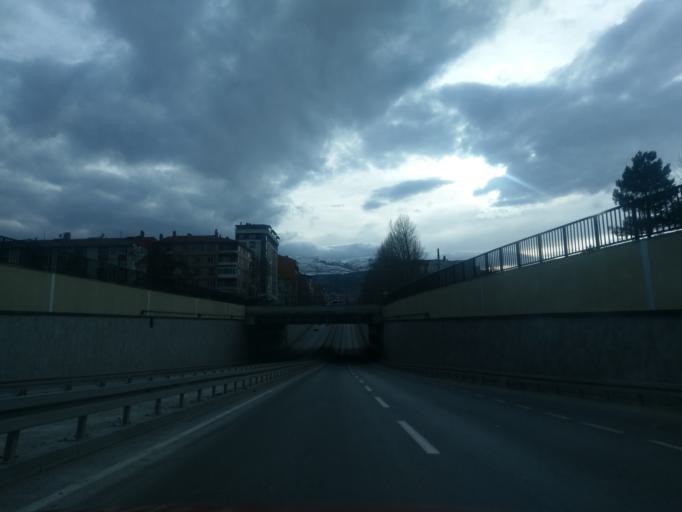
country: TR
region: Kuetahya
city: Kutahya
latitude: 39.4294
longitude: 29.9935
